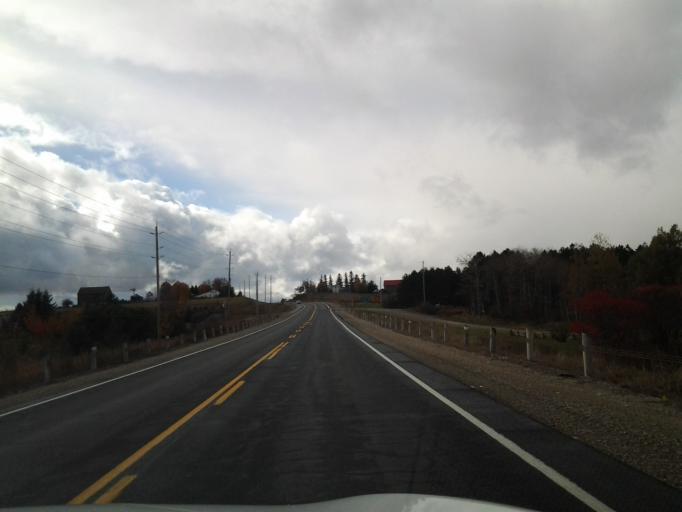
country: CA
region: Ontario
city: Shelburne
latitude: 44.1033
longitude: -80.0790
